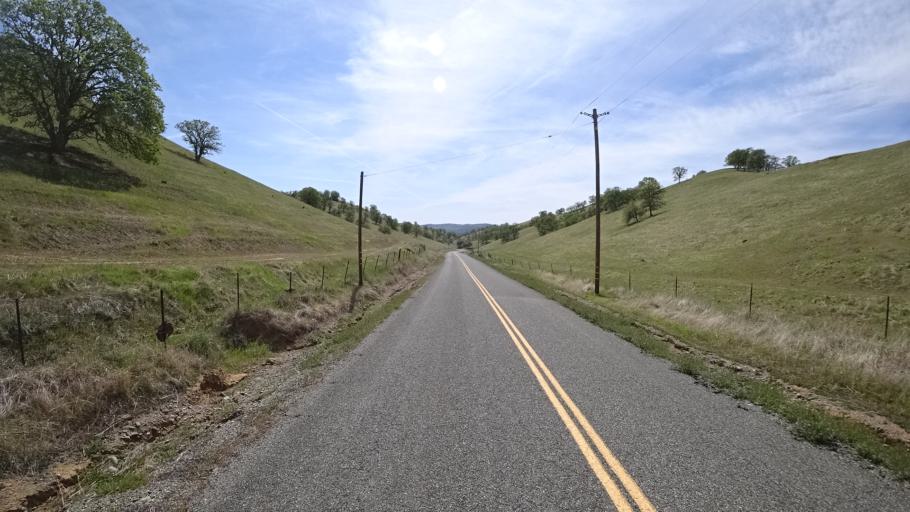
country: US
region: California
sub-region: Glenn County
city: Willows
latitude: 39.5719
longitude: -122.4437
